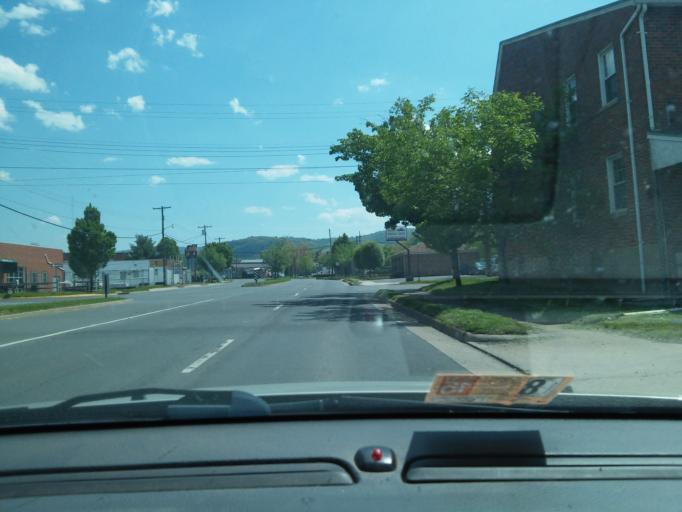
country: US
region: Virginia
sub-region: Warren County
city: Front Royal
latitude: 38.9243
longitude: -78.1914
